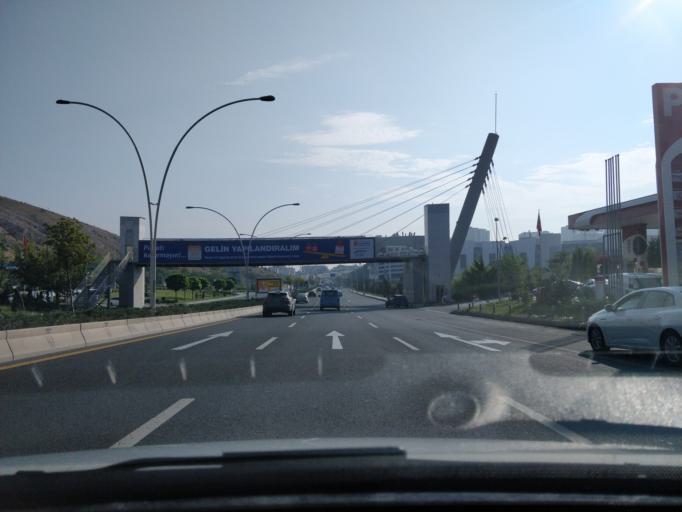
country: TR
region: Ankara
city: Etimesgut
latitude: 39.8992
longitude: 32.6864
